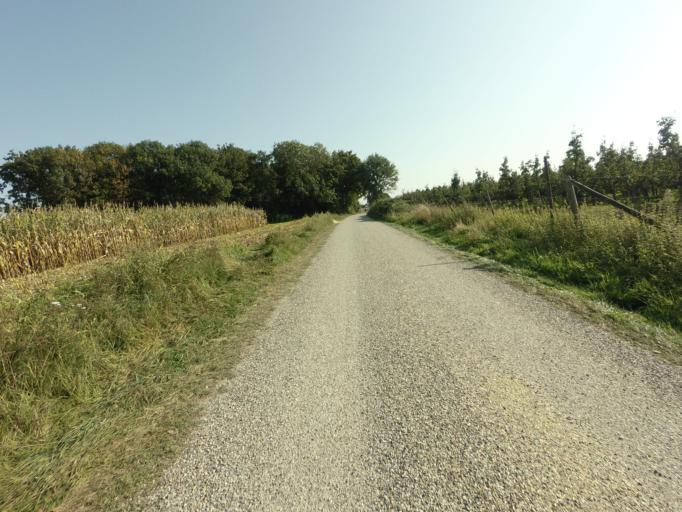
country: NL
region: Limburg
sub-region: Gemeente Maasgouw
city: Maasbracht
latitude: 51.1528
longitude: 5.9008
